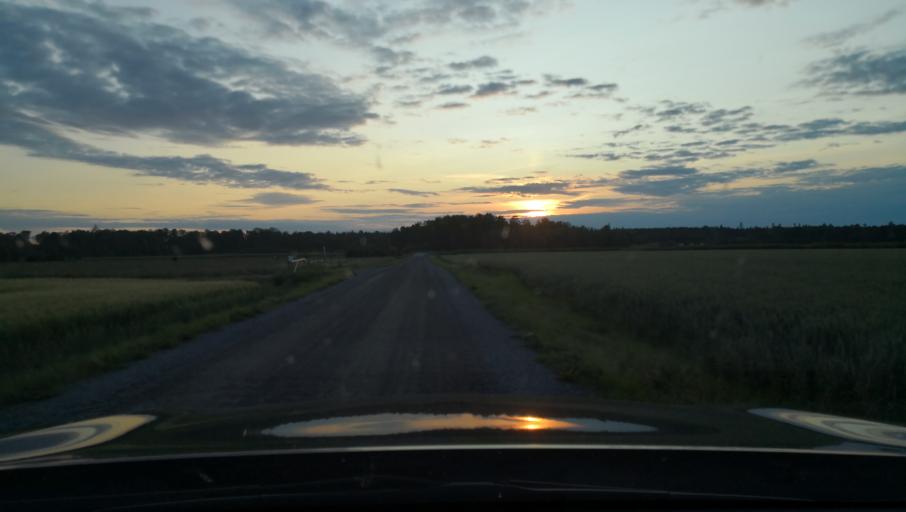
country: SE
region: Uppsala
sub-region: Osthammars Kommun
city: Bjorklinge
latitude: 60.0589
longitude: 17.5864
